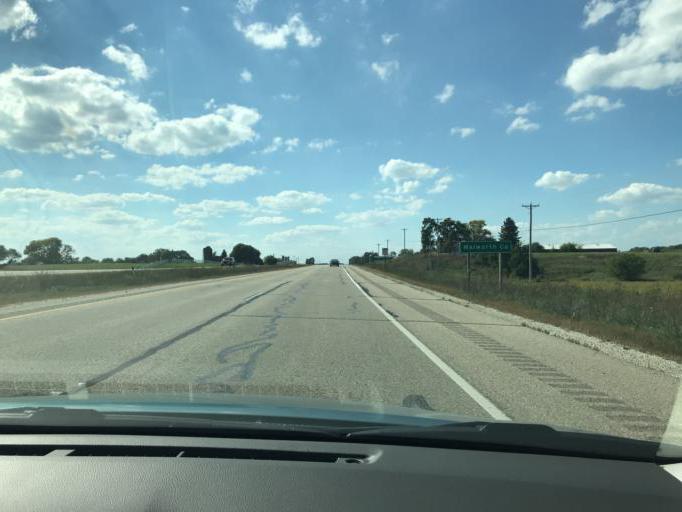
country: US
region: Wisconsin
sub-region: Kenosha County
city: Powers Lake
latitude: 42.5817
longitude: -88.3051
